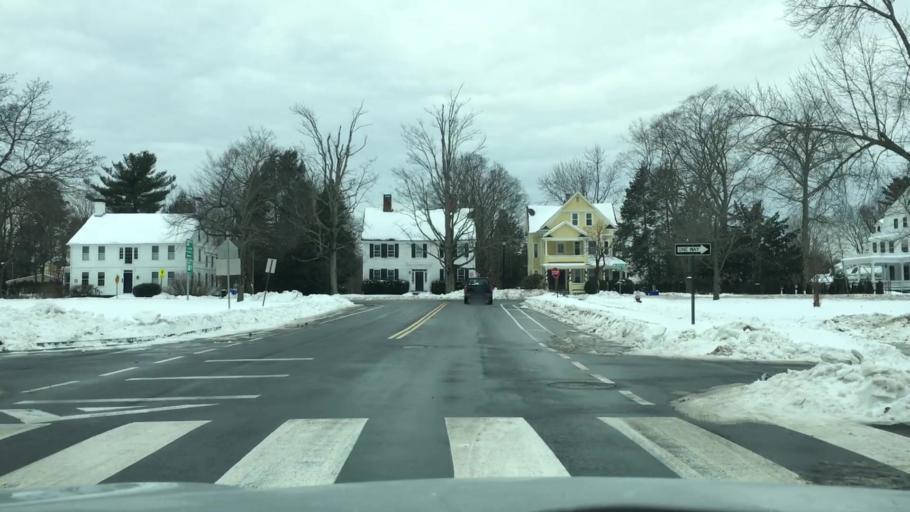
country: US
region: Massachusetts
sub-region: Hampden County
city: Longmeadow
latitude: 42.0504
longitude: -72.5821
